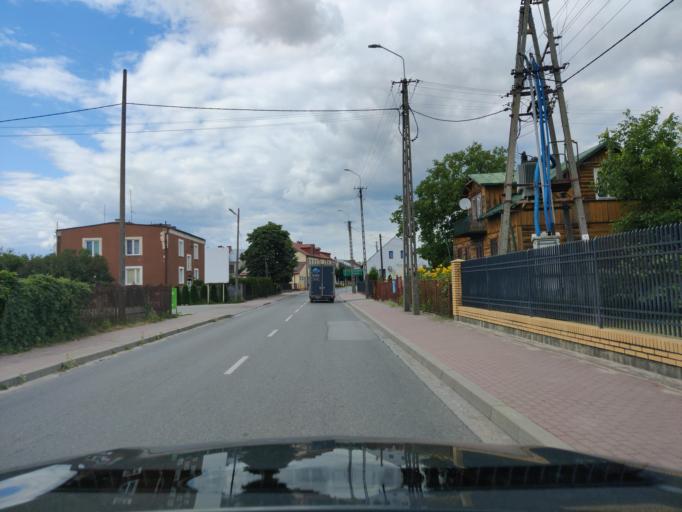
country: PL
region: Masovian Voivodeship
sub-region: Powiat sokolowski
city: Kosow Lacki
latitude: 52.5927
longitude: 22.1475
